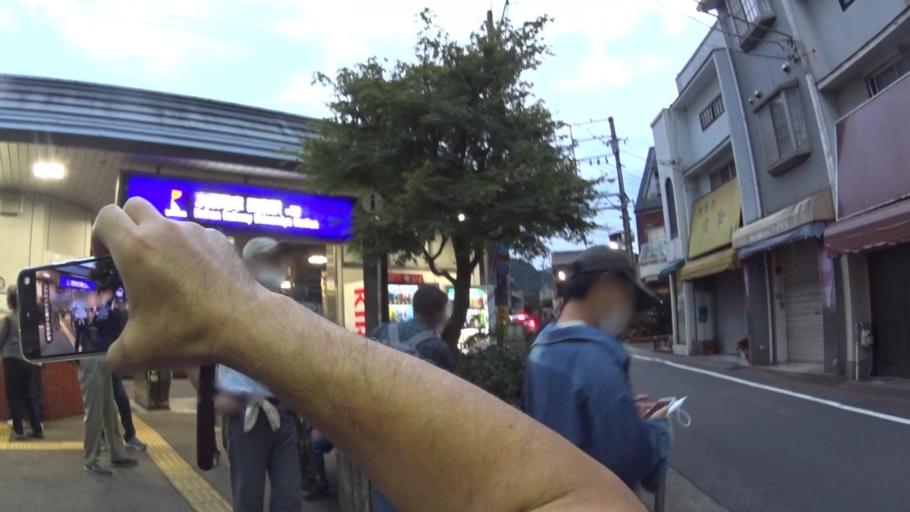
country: JP
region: Osaka
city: Kaizuka
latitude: 34.4413
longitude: 135.2739
